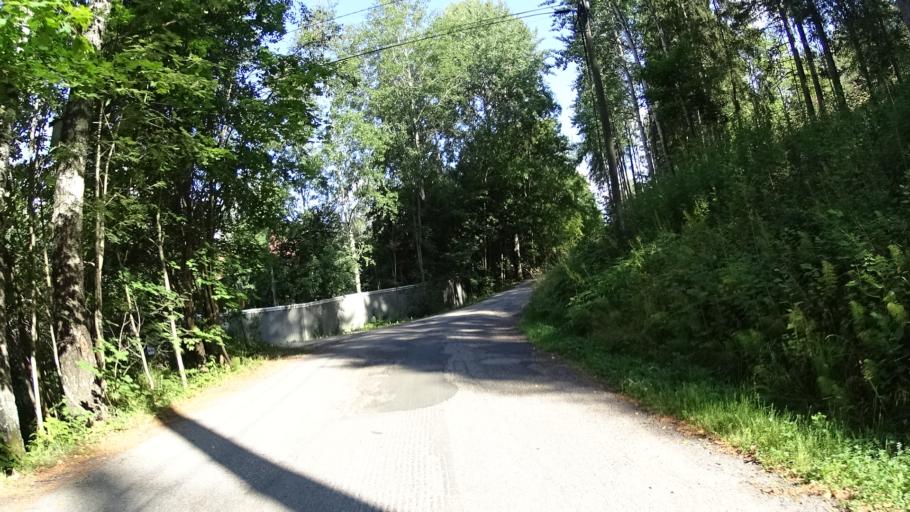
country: FI
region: Uusimaa
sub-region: Helsinki
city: Espoo
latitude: 60.1816
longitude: 24.5912
